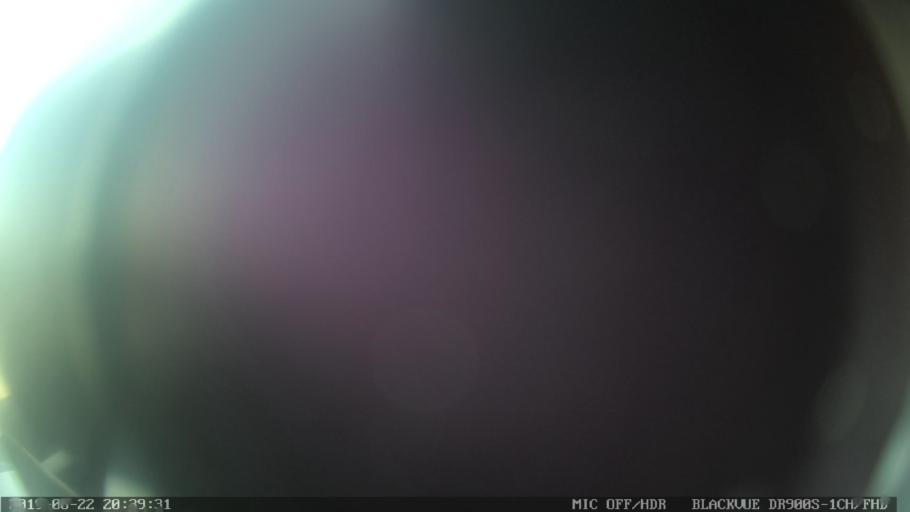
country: PT
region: Castelo Branco
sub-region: Proenca-A-Nova
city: Proenca-a-Nova
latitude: 39.6876
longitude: -7.7722
